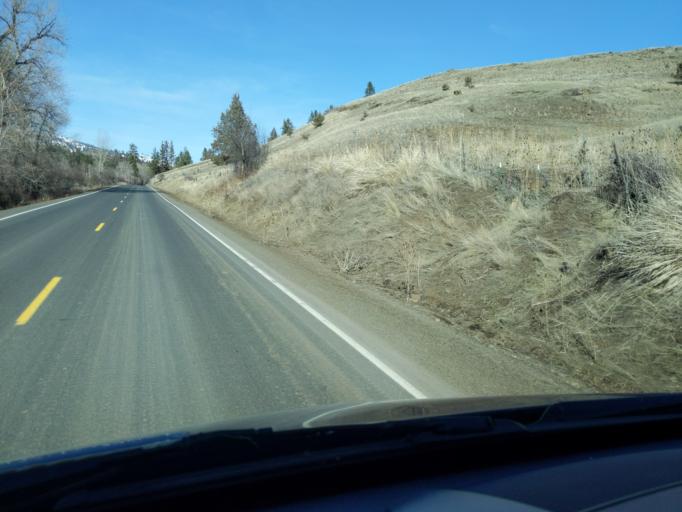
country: US
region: Oregon
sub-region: Grant County
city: John Day
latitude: 44.8494
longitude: -119.0310
